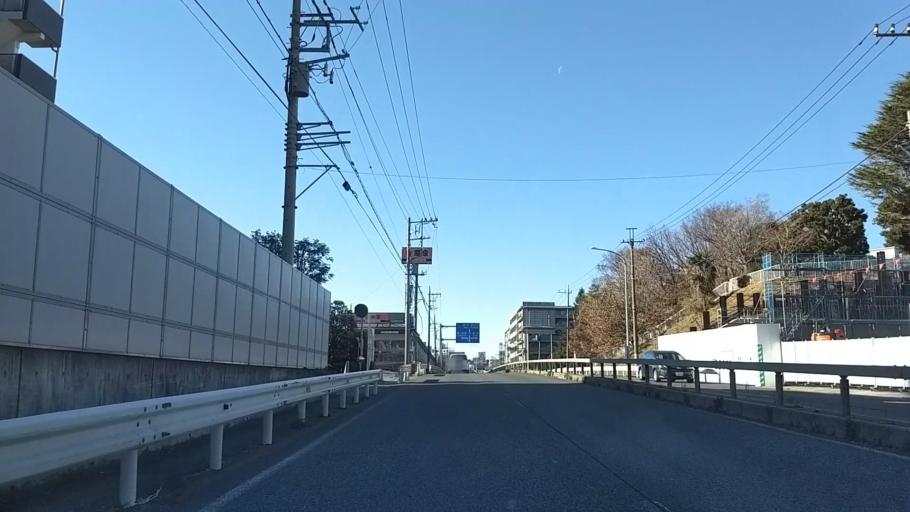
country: JP
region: Tokyo
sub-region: Machida-shi
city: Machida
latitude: 35.5473
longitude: 139.5307
